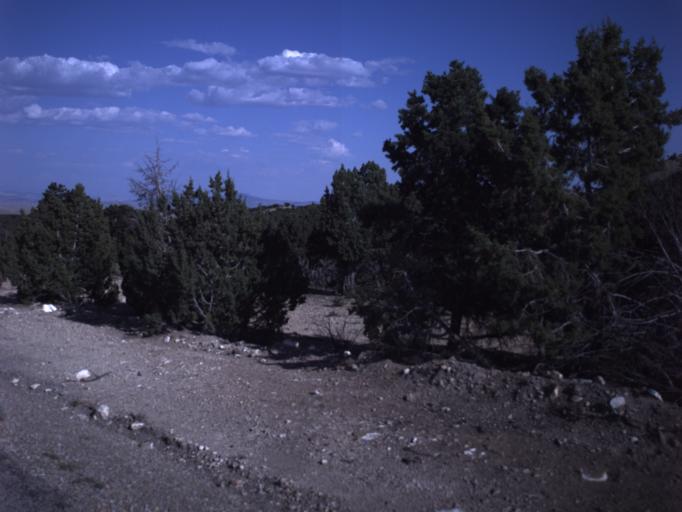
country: US
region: Utah
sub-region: Emery County
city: Huntington
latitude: 39.4870
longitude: -110.9419
